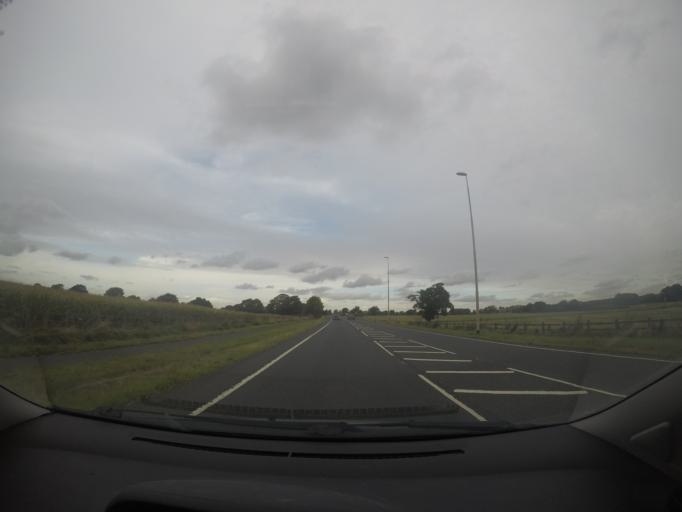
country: GB
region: England
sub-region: North Yorkshire
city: Barlby
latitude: 53.8170
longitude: -1.0436
